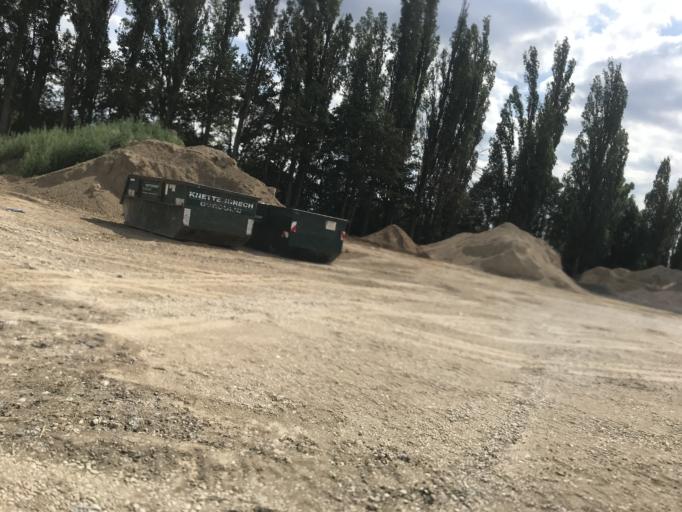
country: DE
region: Hesse
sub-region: Regierungsbezirk Darmstadt
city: Wiesbaden
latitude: 50.0519
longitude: 8.2980
